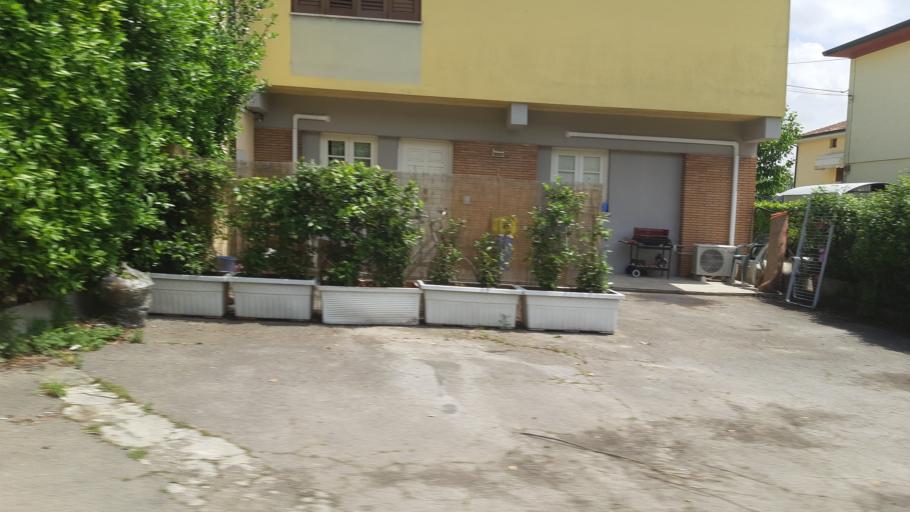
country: IT
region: Tuscany
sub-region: Provincia di Lucca
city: Capannori
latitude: 43.8676
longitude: 10.5623
